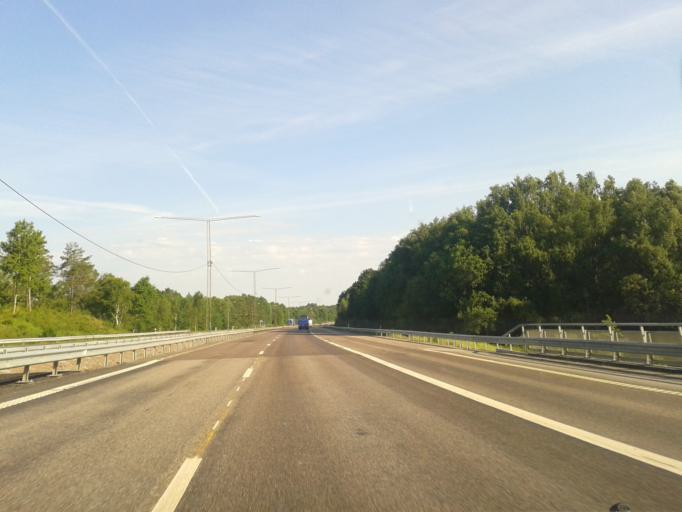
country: SE
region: Vaestra Goetaland
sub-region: Kungalvs Kommun
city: Kode
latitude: 57.9456
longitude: 11.8561
